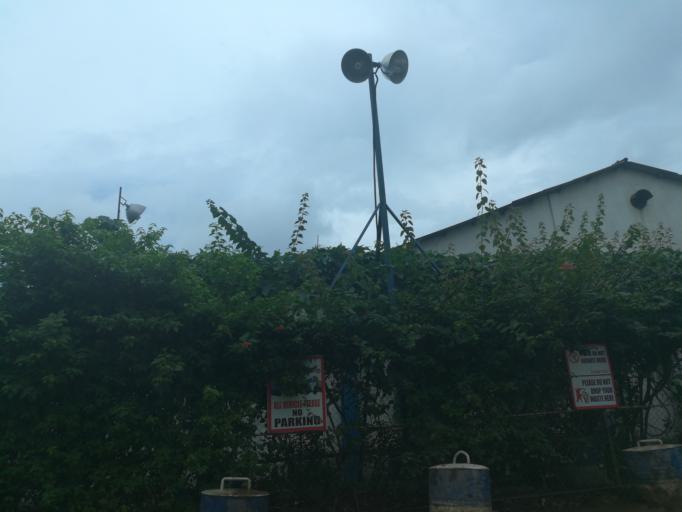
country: NG
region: Lagos
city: Ikeja
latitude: 6.6122
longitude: 3.3417
